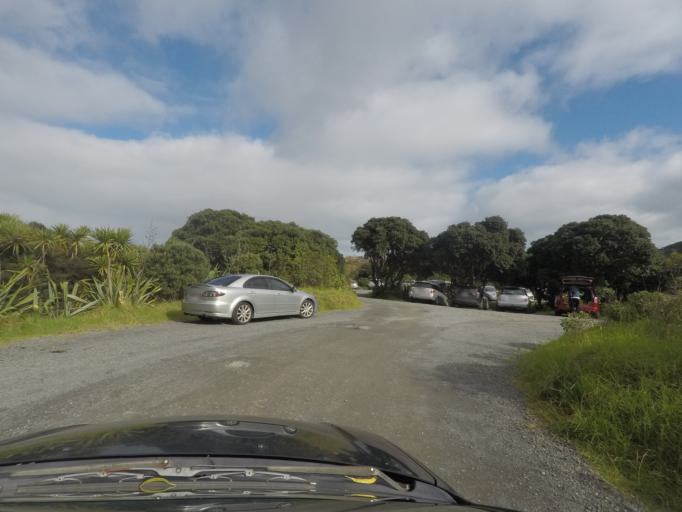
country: NZ
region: Auckland
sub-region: Auckland
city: Muriwai Beach
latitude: -36.8912
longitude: 174.4491
